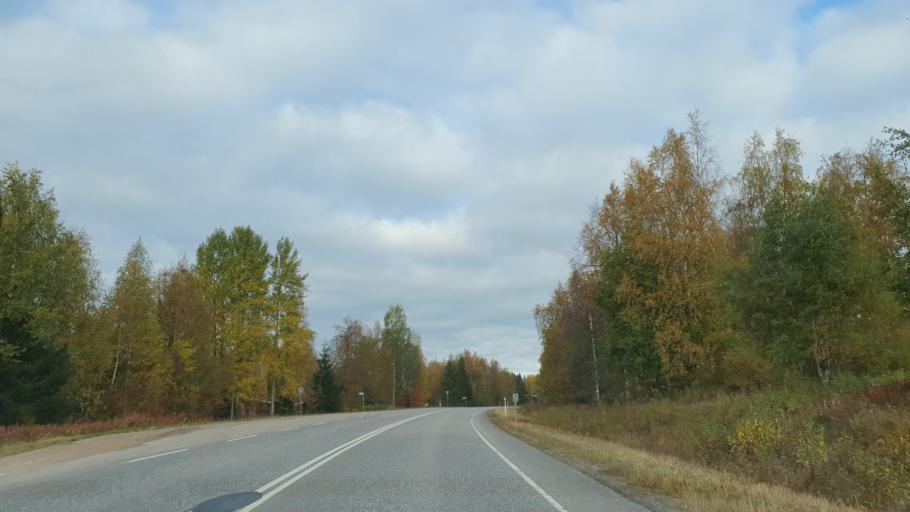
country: FI
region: Kainuu
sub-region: Kehys-Kainuu
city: Puolanka
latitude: 64.8496
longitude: 27.7669
